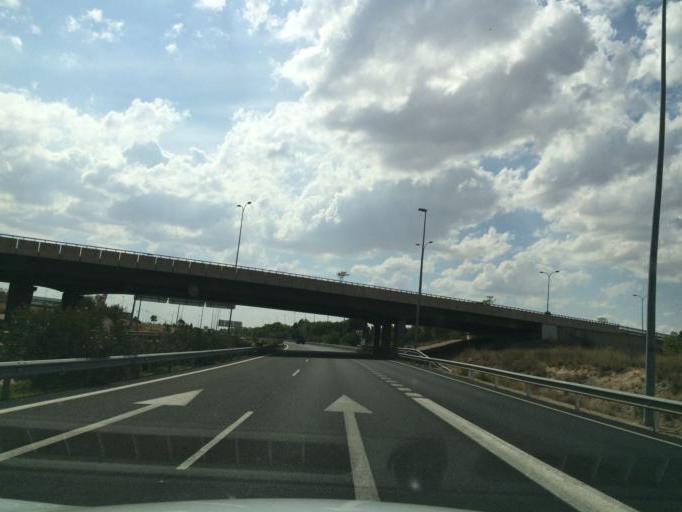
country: ES
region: Castille-La Mancha
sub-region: Provincia de Albacete
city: Albacete
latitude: 39.0118
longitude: -1.8741
